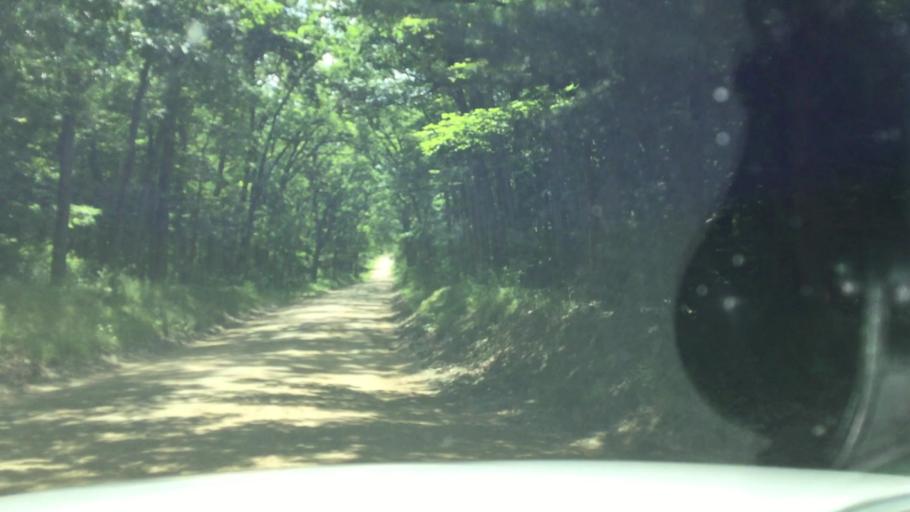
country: US
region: Michigan
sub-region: Ionia County
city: Belding
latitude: 43.1197
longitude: -85.2134
